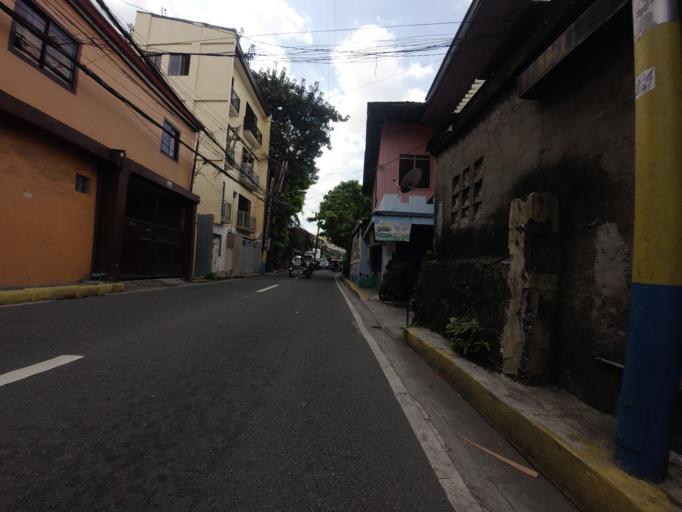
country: PH
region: Metro Manila
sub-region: San Juan
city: San Juan
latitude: 14.5893
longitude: 121.0303
